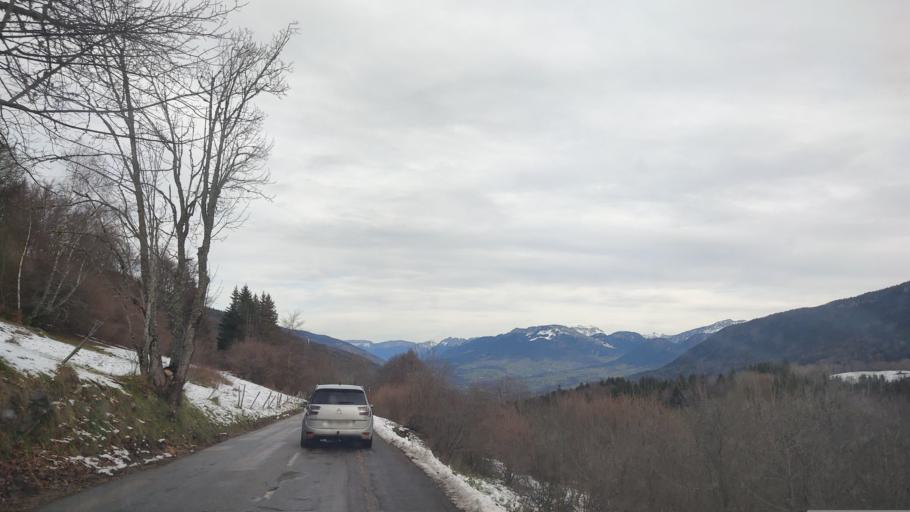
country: FR
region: Rhone-Alpes
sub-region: Departement de la Savoie
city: Mery
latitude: 45.6589
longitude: 6.0323
